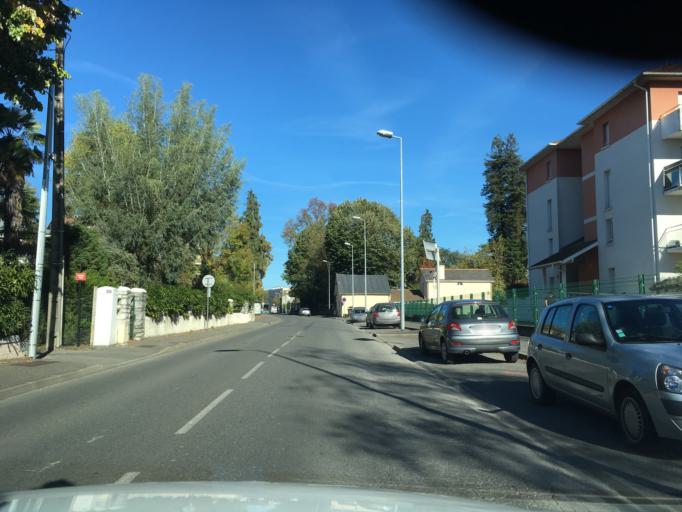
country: FR
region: Aquitaine
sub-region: Departement des Pyrenees-Atlantiques
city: Pau
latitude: 43.3074
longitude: -0.3466
